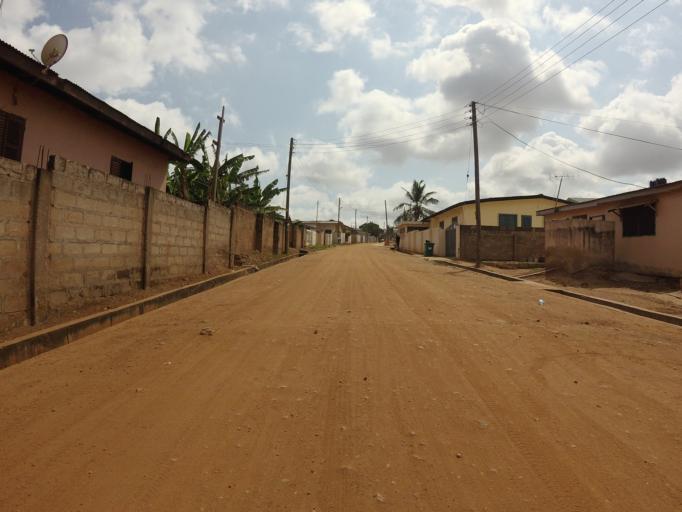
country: GH
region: Greater Accra
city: Dome
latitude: 5.6173
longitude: -0.2452
